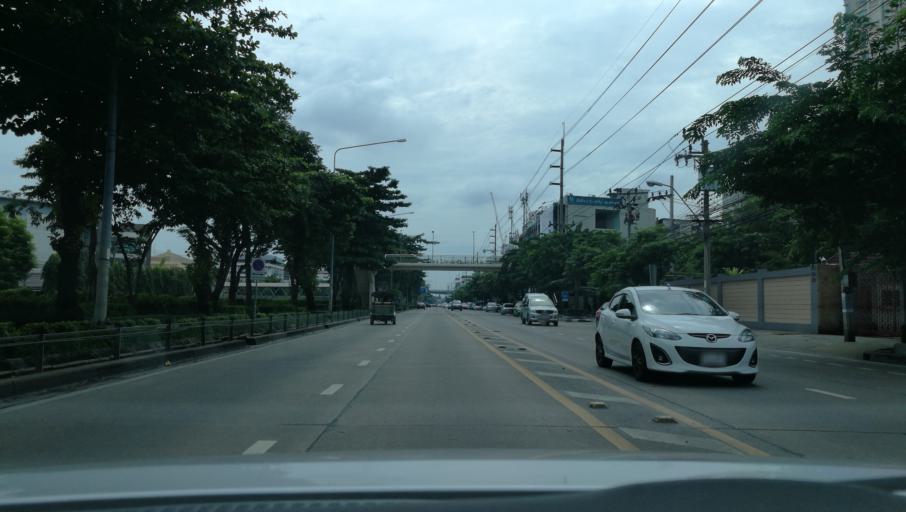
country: TH
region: Bangkok
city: Bang Sue
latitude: 13.8124
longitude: 100.5347
